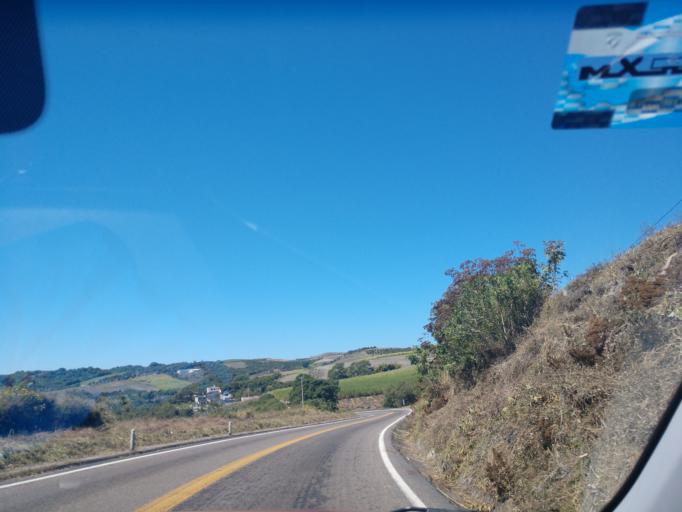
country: MX
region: Nayarit
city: Xalisco
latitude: 21.3699
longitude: -104.9084
